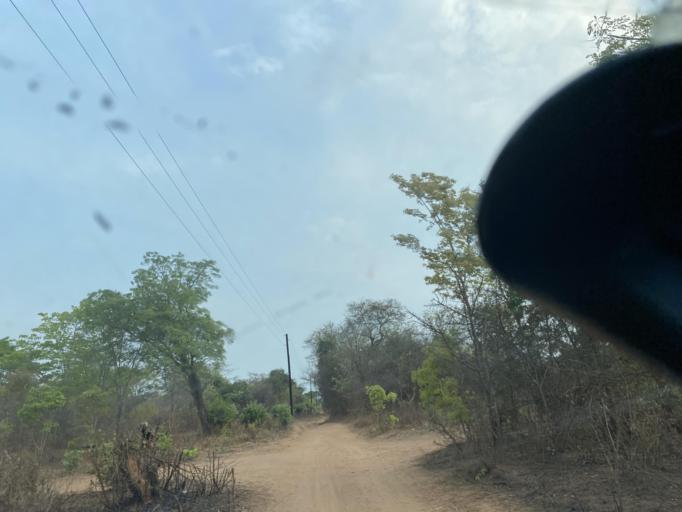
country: ZM
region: Lusaka
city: Chongwe
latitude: -15.2017
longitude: 28.4962
